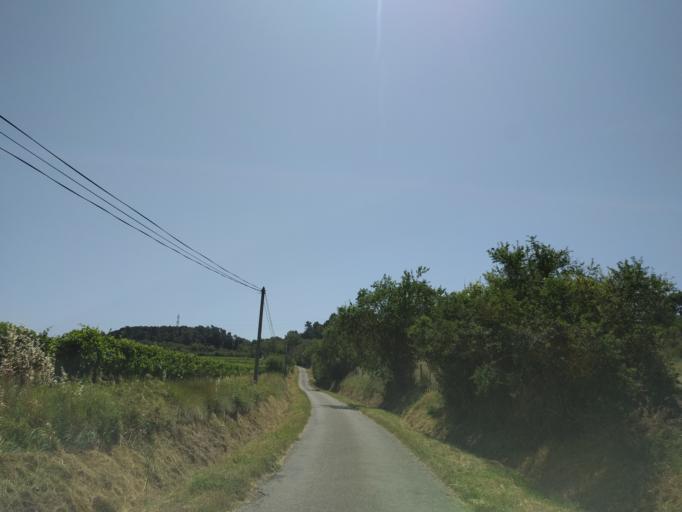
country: FR
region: Languedoc-Roussillon
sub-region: Departement de l'Aude
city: Cazilhac
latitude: 43.1994
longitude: 2.3752
